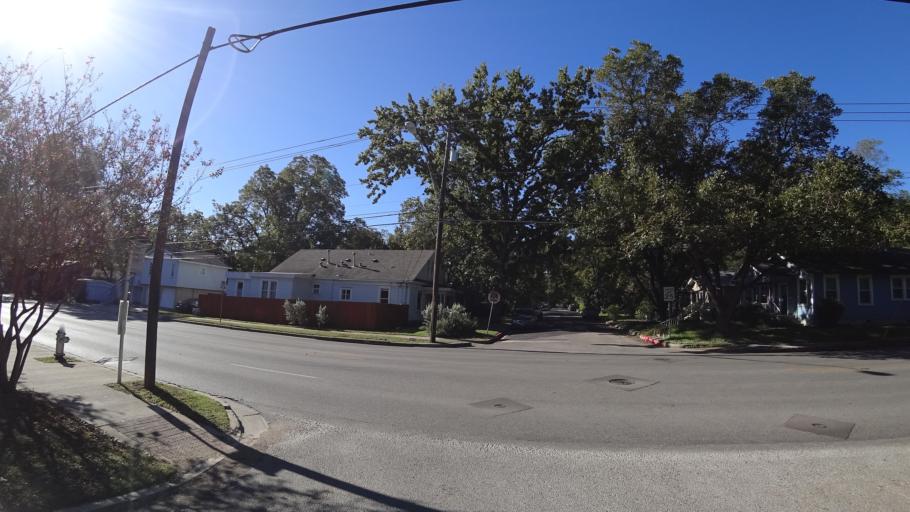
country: US
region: Texas
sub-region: Travis County
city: Austin
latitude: 30.3092
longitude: -97.7292
